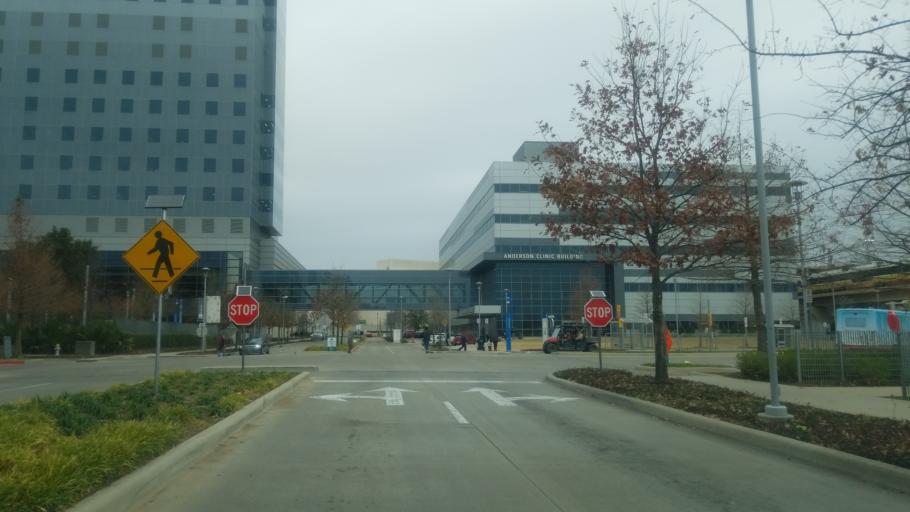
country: US
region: Texas
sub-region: Dallas County
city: Dallas
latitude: 32.8121
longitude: -96.8338
